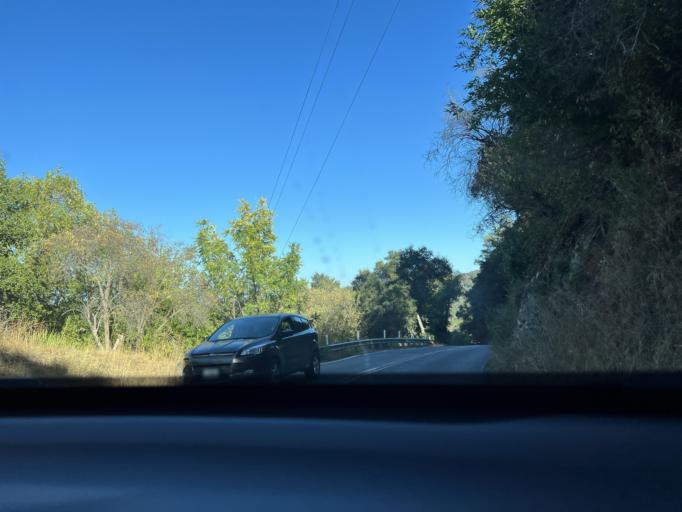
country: US
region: California
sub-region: Santa Clara County
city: Loyola
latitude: 37.2959
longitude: -122.0883
